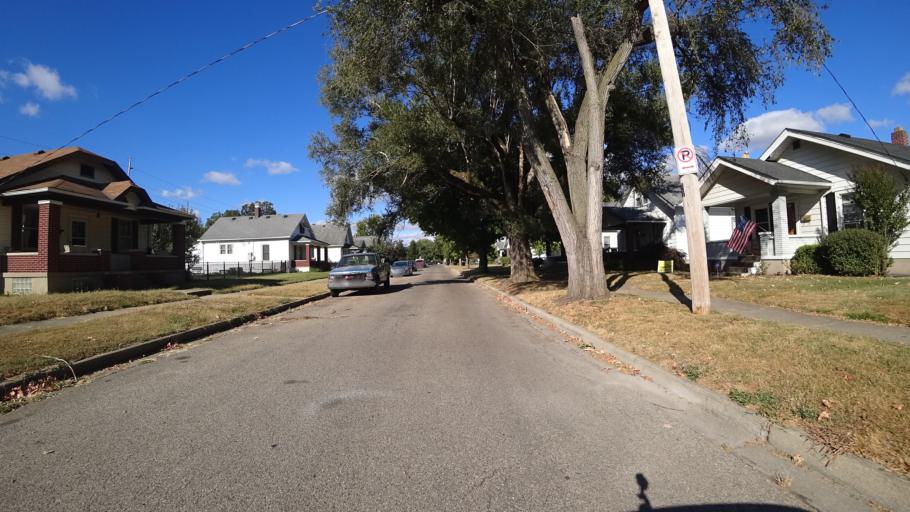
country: US
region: Ohio
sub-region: Butler County
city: Fairfield
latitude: 39.3676
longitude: -84.5512
